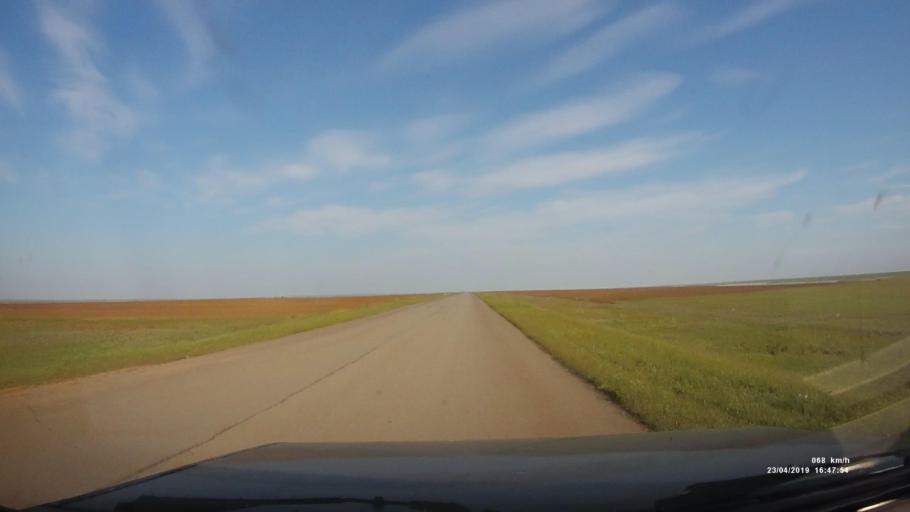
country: RU
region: Kalmykiya
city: Priyutnoye
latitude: 46.3371
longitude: 43.2541
